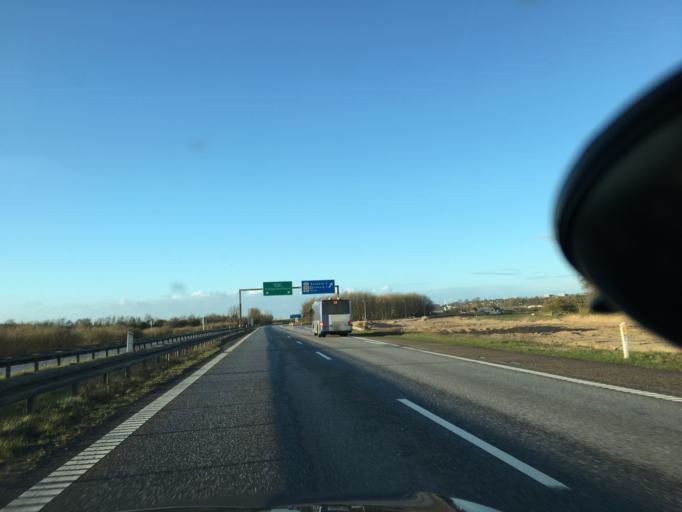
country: DK
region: North Denmark
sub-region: Alborg Kommune
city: Aalborg
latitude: 57.0010
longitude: 9.9080
